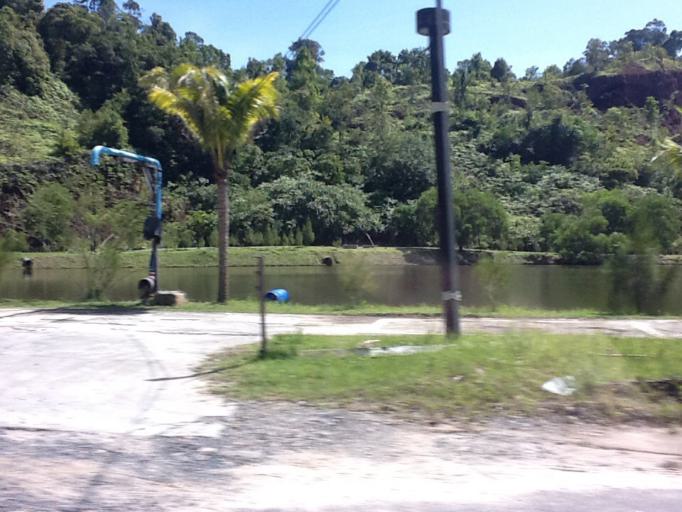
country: TH
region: Phuket
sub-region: Amphoe Kathu
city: Kathu
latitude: 7.9366
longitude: 98.3490
